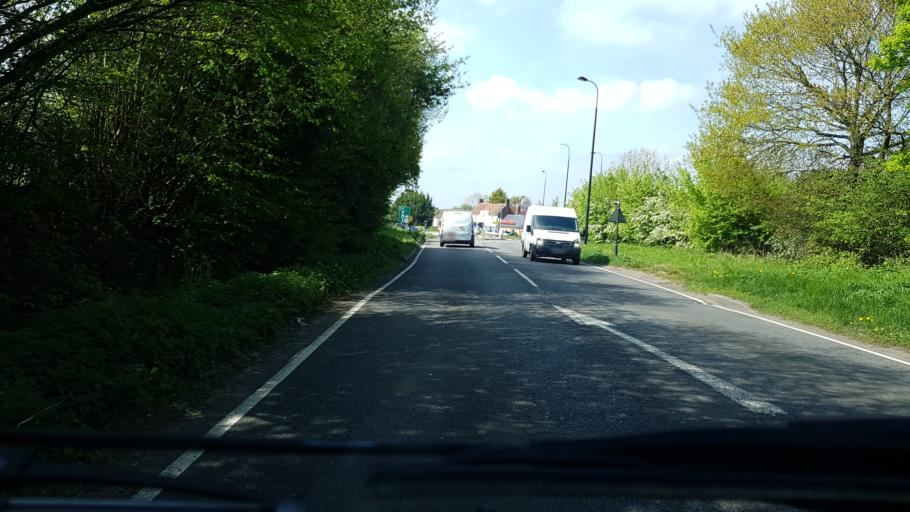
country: GB
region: England
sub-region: Kent
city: Pembury
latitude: 51.1336
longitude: 0.3537
